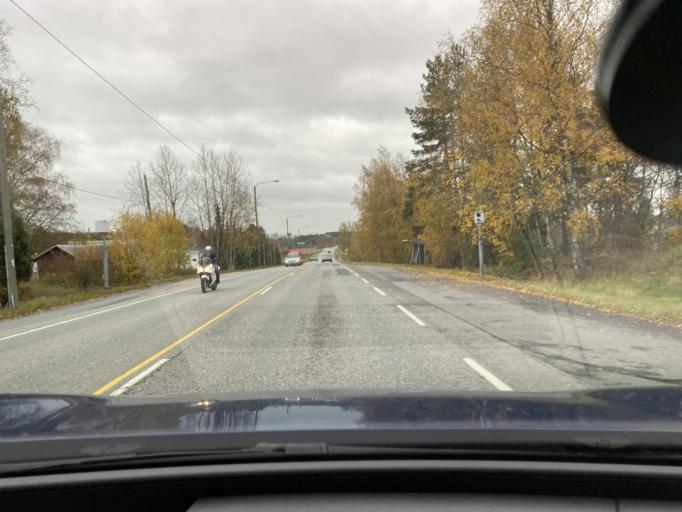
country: FI
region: Varsinais-Suomi
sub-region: Vakka-Suomi
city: Pyhaeranta
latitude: 60.9851
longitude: 21.5877
